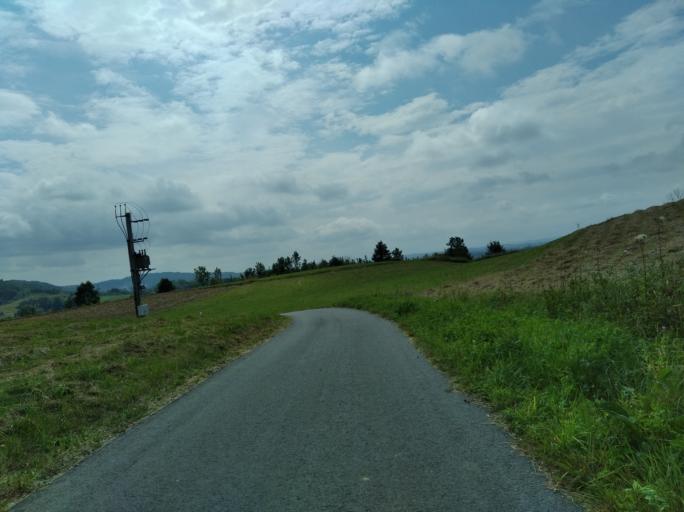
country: PL
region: Subcarpathian Voivodeship
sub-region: Powiat krosnienski
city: Leki
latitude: 49.8096
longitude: 21.6676
